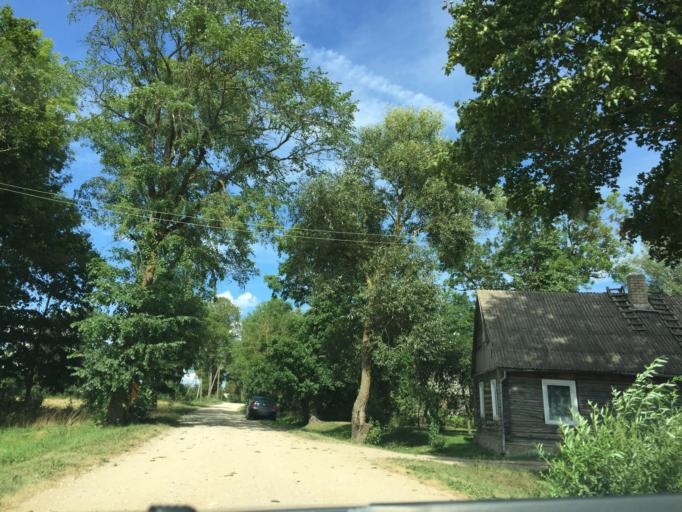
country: LT
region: Siauliu apskritis
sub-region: Joniskis
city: Joniskis
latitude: 56.3459
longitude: 23.6232
